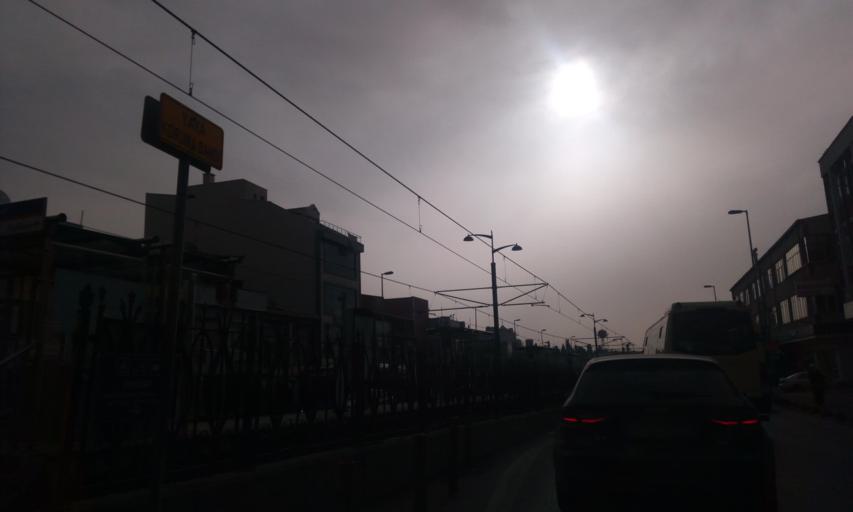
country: TR
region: Istanbul
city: Istanbul
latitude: 41.0374
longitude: 28.9230
